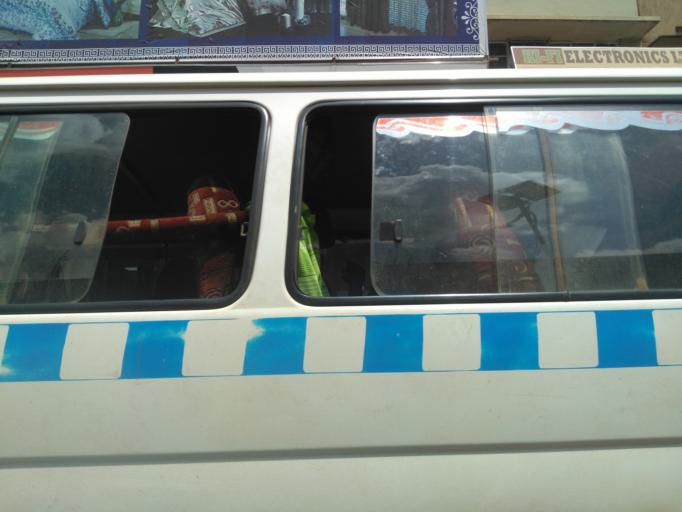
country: UG
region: Central Region
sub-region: Kampala District
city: Kampala
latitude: 0.3170
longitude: 32.5760
